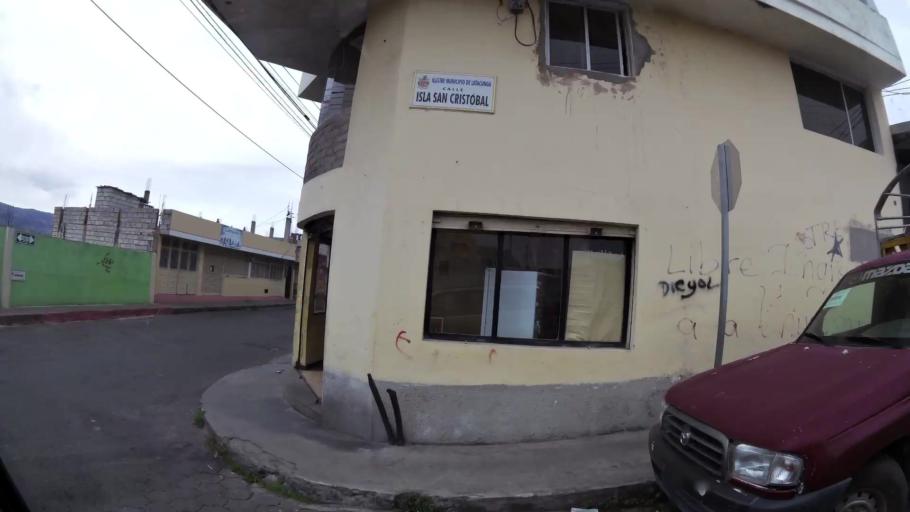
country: EC
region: Cotopaxi
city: Latacunga
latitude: -0.9308
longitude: -78.6100
